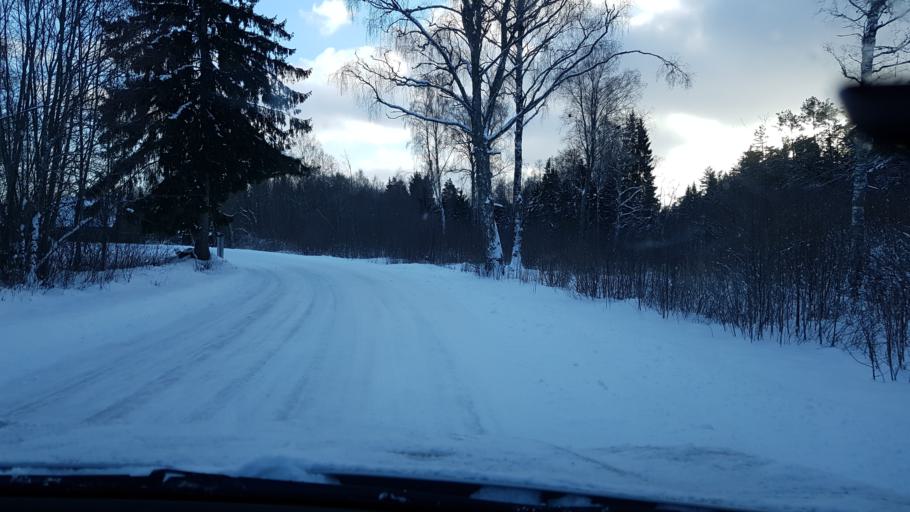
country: EE
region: Harju
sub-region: Nissi vald
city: Turba
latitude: 59.1532
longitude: 24.1452
